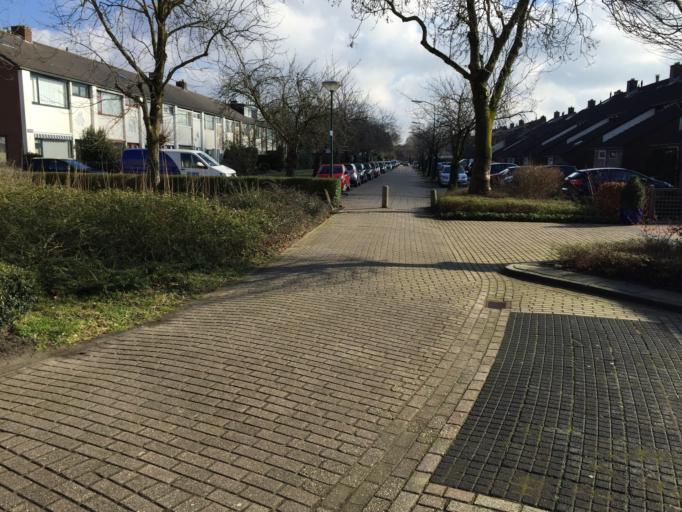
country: NL
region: Utrecht
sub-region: Gemeente Montfoort
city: Montfoort
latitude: 52.0915
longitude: 4.9552
